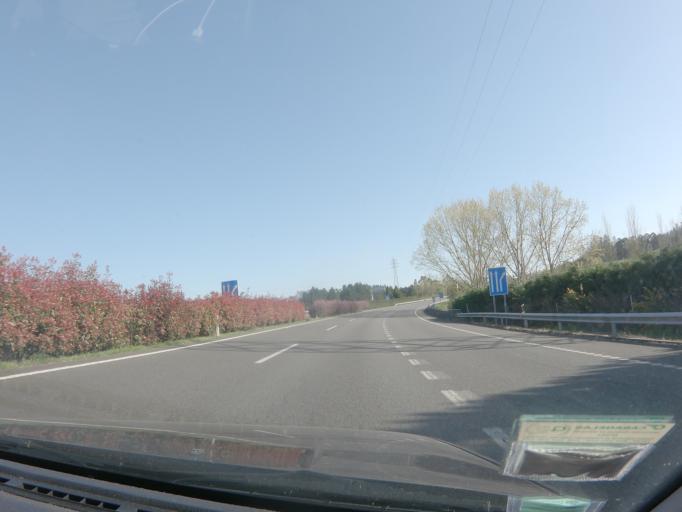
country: ES
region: Galicia
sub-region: Provincia da Coruna
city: Betanzos
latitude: 43.2683
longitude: -8.2299
